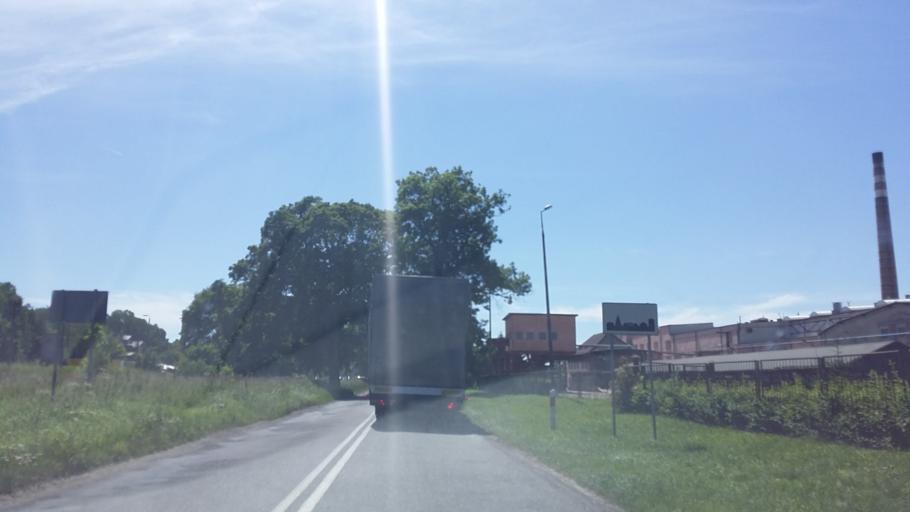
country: PL
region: West Pomeranian Voivodeship
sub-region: Powiat lobeski
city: Lobez
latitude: 53.6441
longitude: 15.6355
